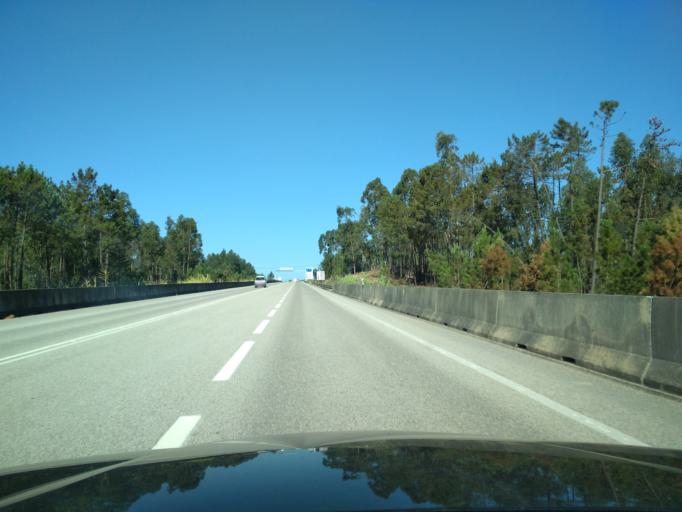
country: PT
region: Leiria
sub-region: Pombal
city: Lourical
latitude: 39.9882
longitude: -8.7728
